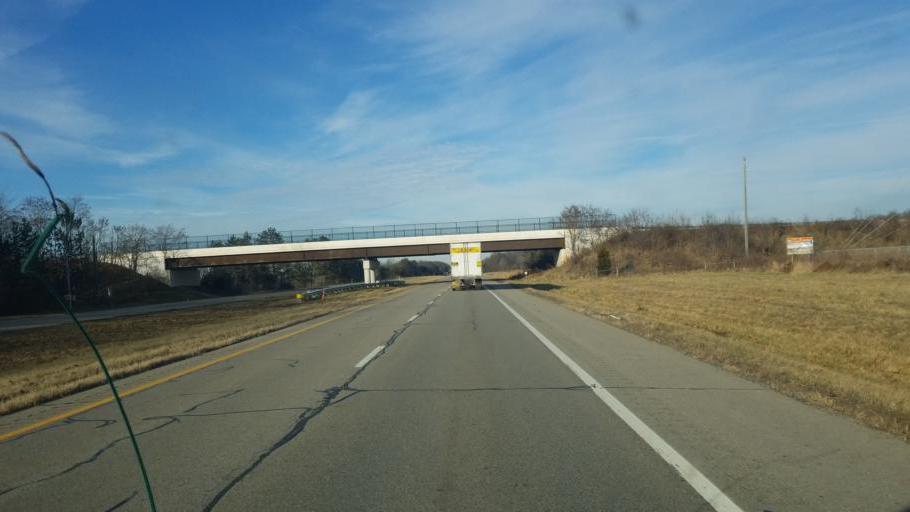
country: US
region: Ohio
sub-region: Ashtabula County
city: Orwell
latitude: 41.5053
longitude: -80.7131
